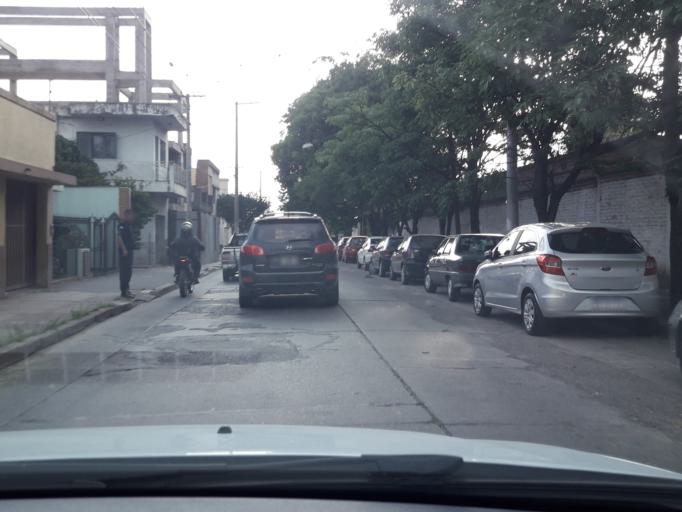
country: AR
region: Jujuy
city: San Salvador de Jujuy
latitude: -24.1907
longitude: -65.3102
